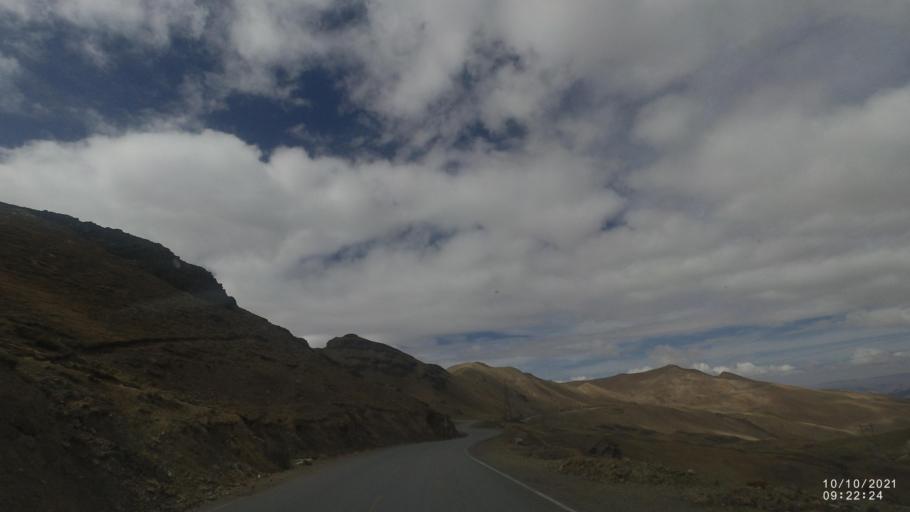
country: BO
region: La Paz
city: Quime
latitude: -17.0766
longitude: -67.2989
